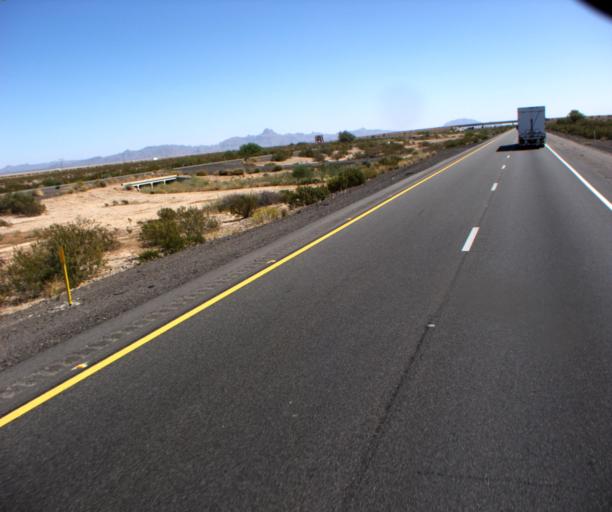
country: US
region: Arizona
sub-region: La Paz County
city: Salome
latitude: 33.5700
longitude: -113.3614
